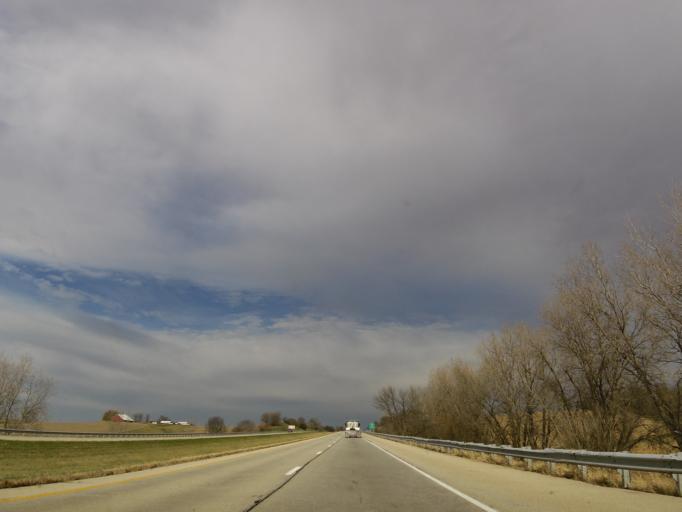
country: US
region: Illinois
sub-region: Henry County
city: Orion
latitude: 41.2753
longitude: -90.3327
